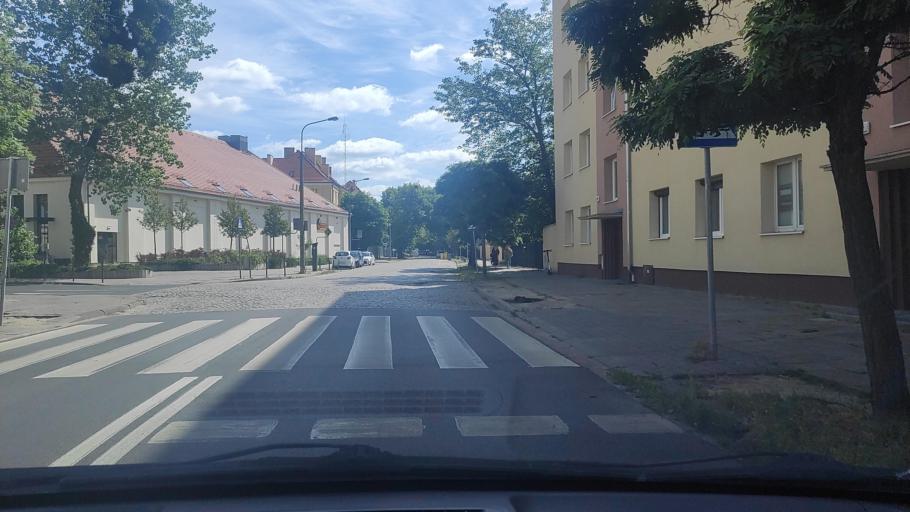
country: PL
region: Greater Poland Voivodeship
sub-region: Poznan
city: Poznan
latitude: 52.4052
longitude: 16.8927
